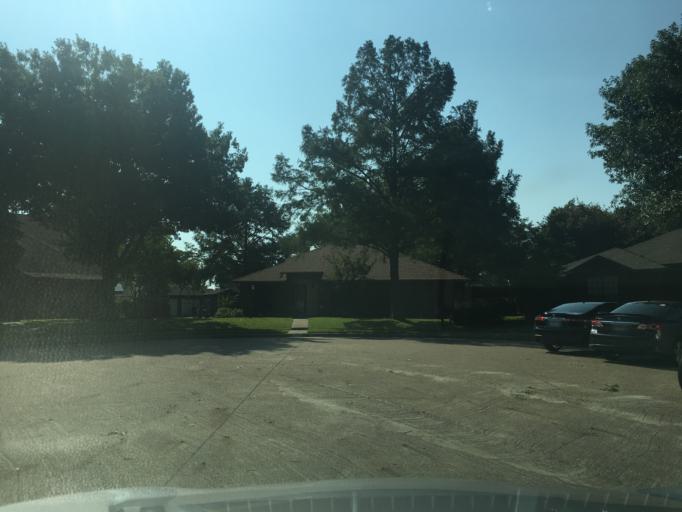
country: US
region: Texas
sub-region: Dallas County
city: Garland
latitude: 32.9462
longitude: -96.6245
